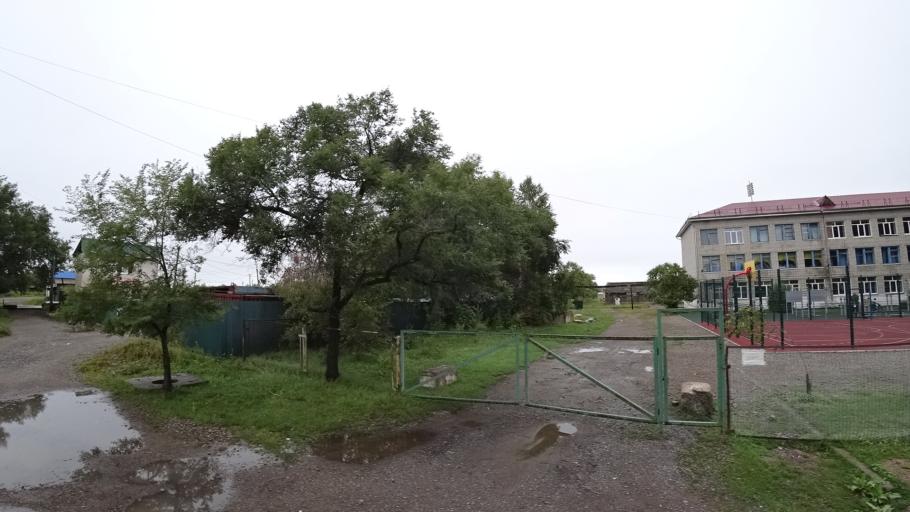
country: RU
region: Primorskiy
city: Monastyrishche
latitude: 44.2065
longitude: 132.4453
